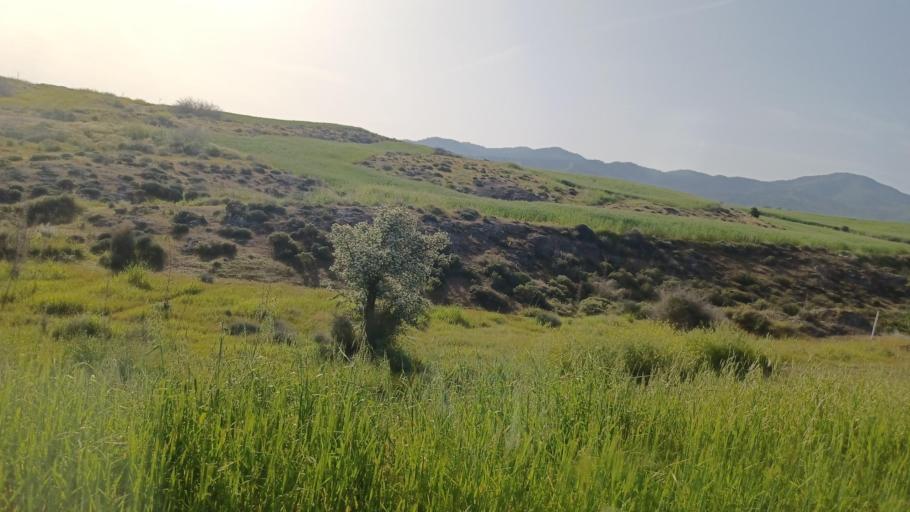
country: CY
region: Lefkosia
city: Lefka
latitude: 35.0884
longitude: 32.9408
